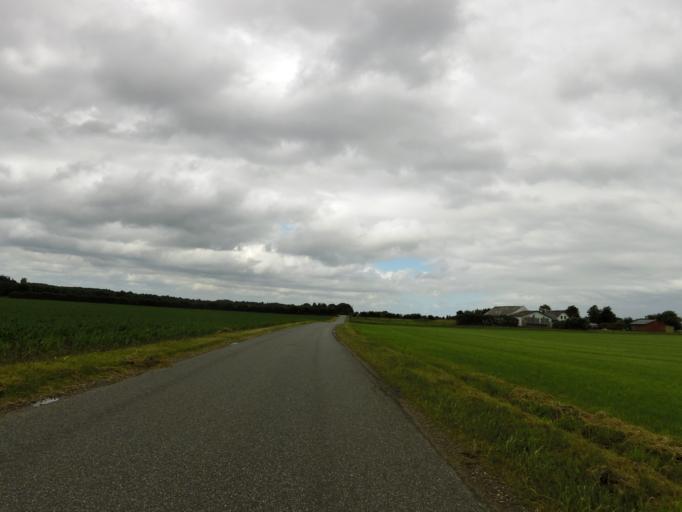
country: DK
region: South Denmark
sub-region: Kolding Kommune
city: Vamdrup
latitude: 55.3454
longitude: 9.1987
